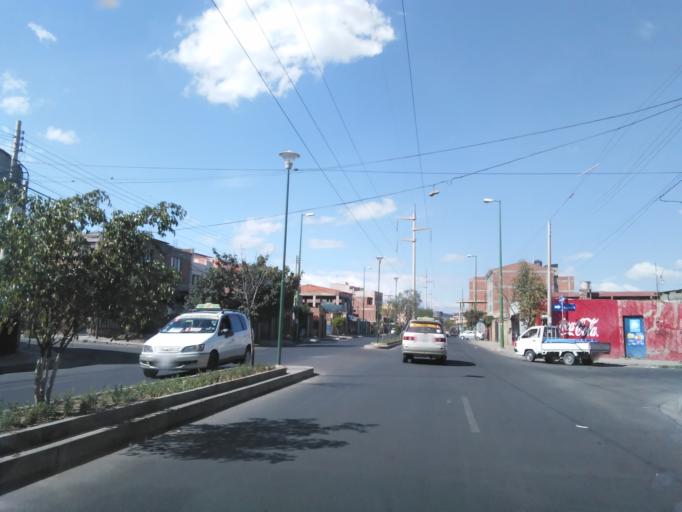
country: BO
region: Cochabamba
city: Cochabamba
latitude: -17.3964
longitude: -66.1801
